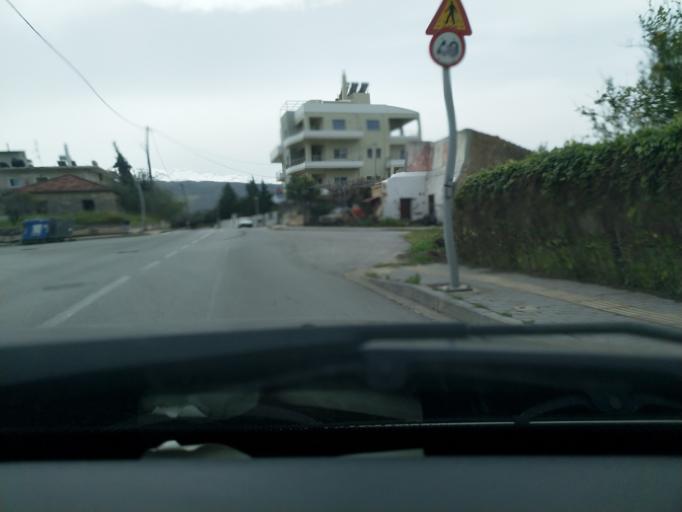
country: GR
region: Crete
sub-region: Nomos Chanias
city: Chania
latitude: 35.4996
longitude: 24.0216
